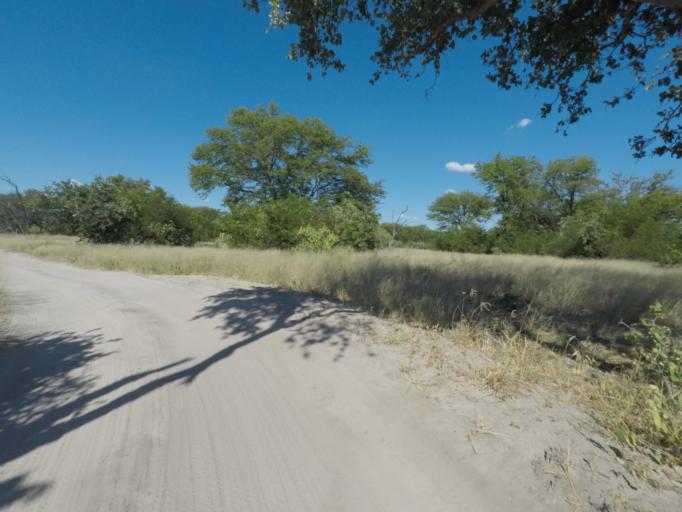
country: BW
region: North West
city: Maun
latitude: -19.4256
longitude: 23.6419
